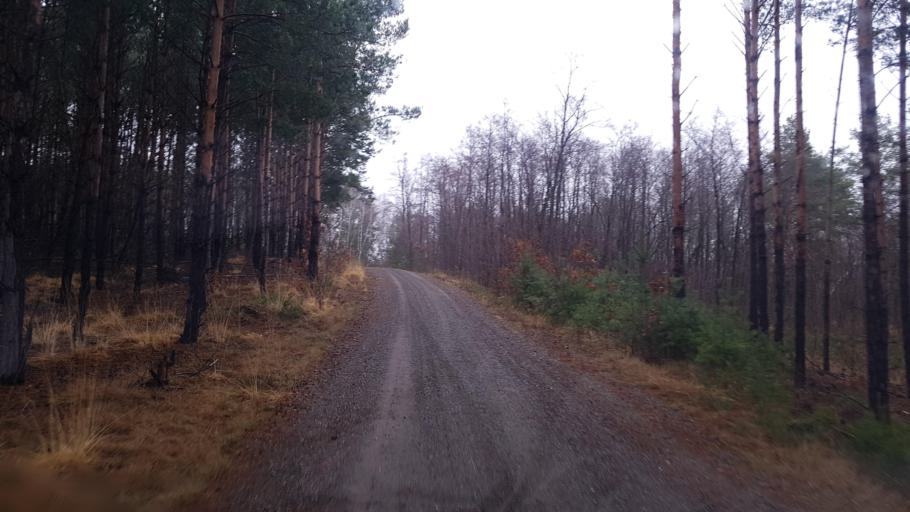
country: DE
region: Brandenburg
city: Lauchhammer
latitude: 51.5267
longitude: 13.7087
